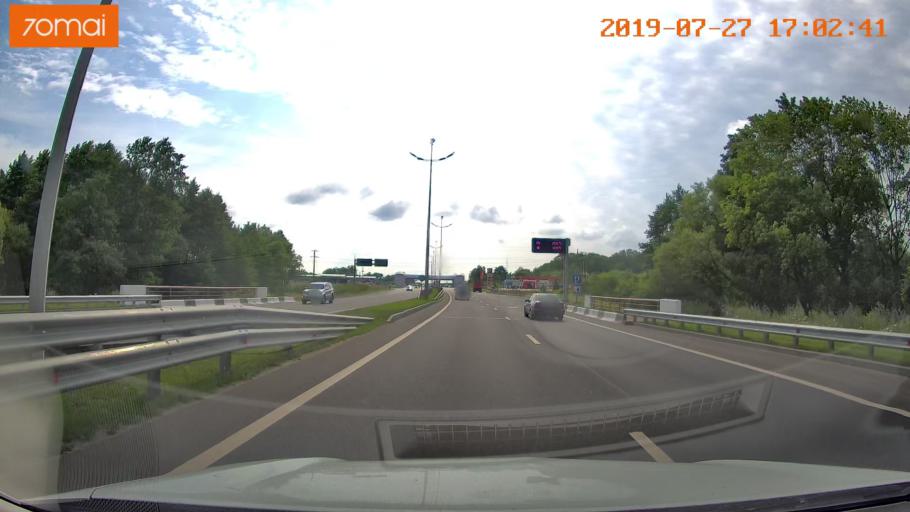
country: RU
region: Kaliningrad
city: Bol'shoe Isakovo
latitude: 54.7057
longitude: 20.6131
